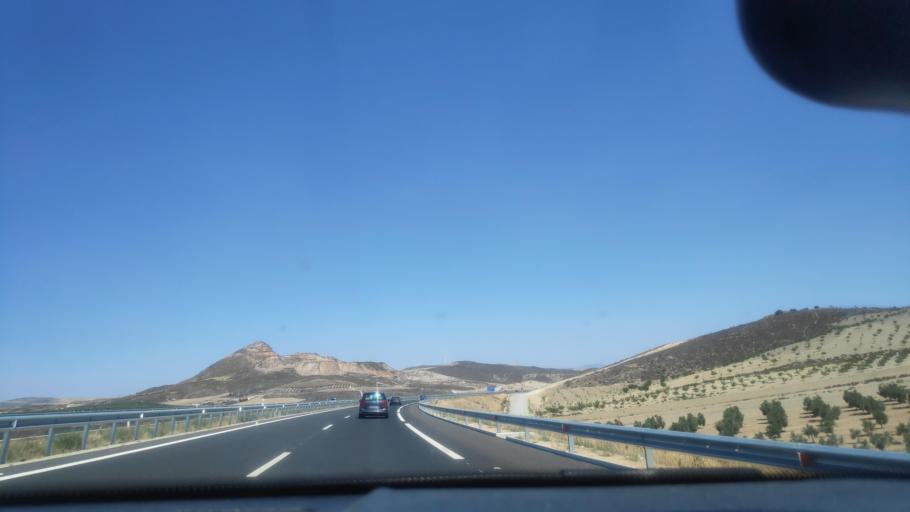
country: ES
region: Andalusia
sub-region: Provincia de Granada
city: Alhendin
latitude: 37.0902
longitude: -3.6704
